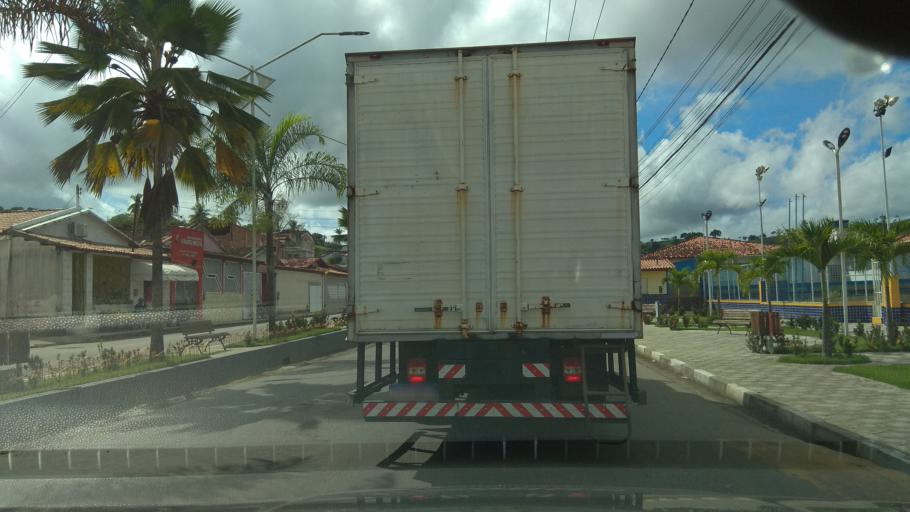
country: BR
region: Bahia
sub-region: Mutuipe
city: Mutuipe
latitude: -13.1805
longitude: -39.4184
